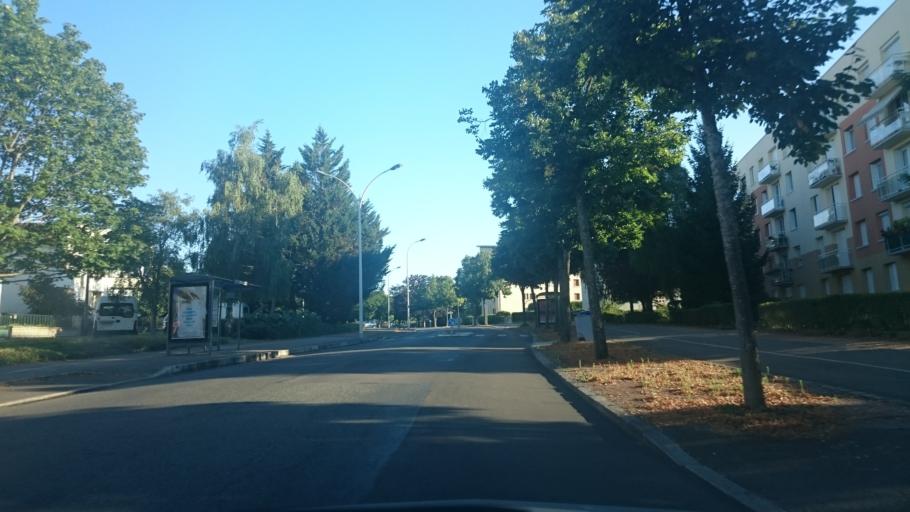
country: FR
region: Bourgogne
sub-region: Departement de la Cote-d'Or
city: Saint-Apollinaire
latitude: 47.3331
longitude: 5.0631
